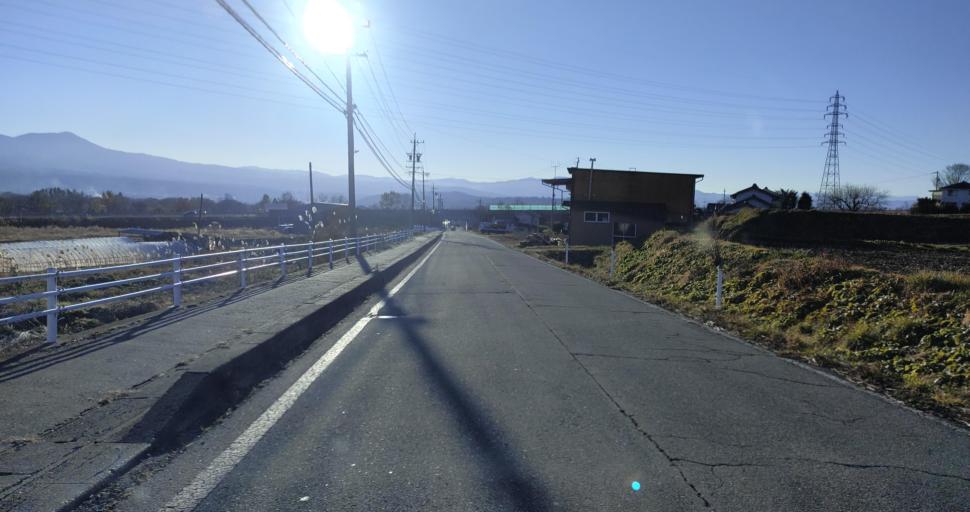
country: JP
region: Nagano
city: Komoro
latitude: 36.3255
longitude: 138.4731
